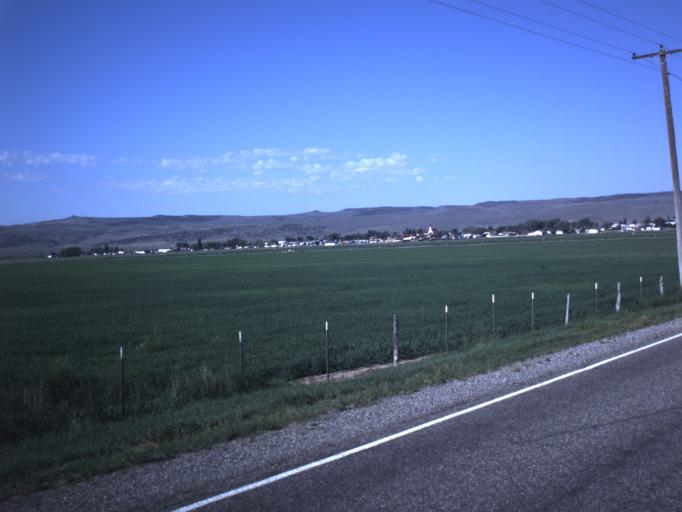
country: US
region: Utah
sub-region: Wayne County
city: Loa
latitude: 38.4116
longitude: -111.6248
